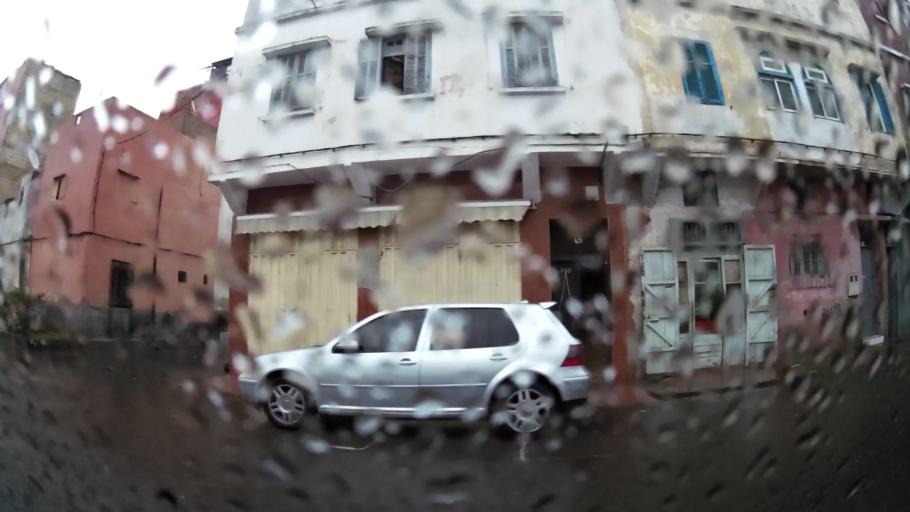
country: MA
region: Grand Casablanca
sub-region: Casablanca
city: Casablanca
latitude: 33.5638
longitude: -7.6032
